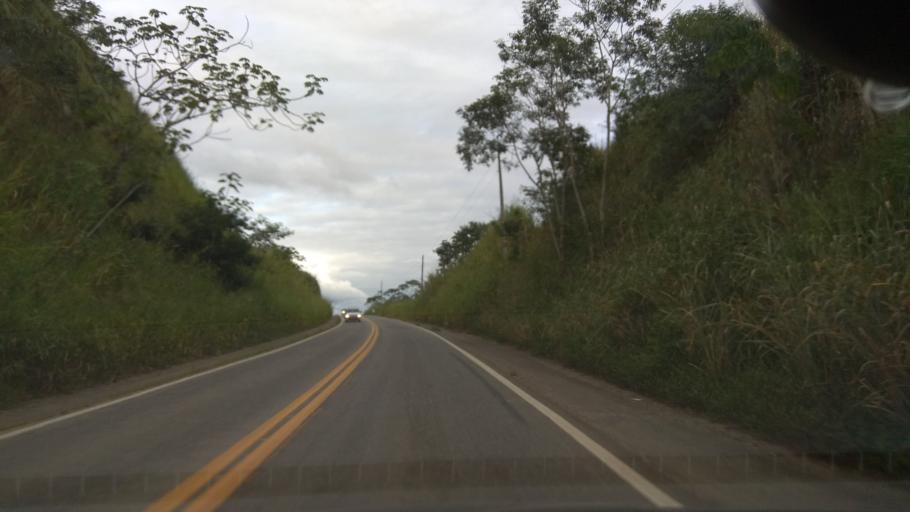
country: BR
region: Bahia
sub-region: Ipiau
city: Ipiau
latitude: -14.1536
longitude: -39.6980
